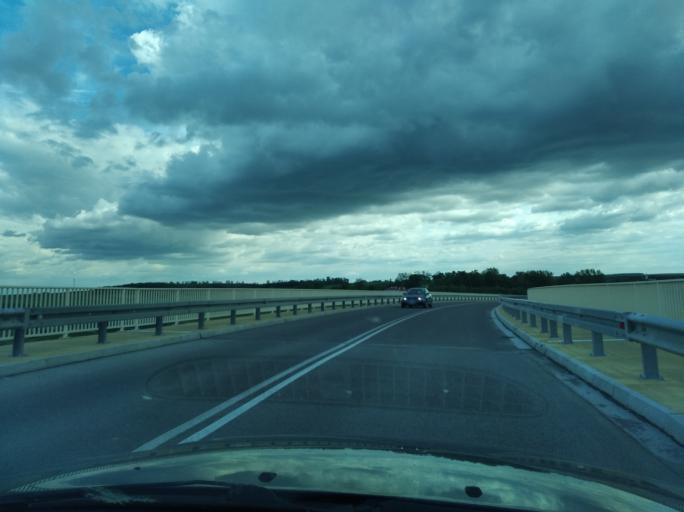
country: PL
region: Subcarpathian Voivodeship
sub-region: Powiat jaroslawski
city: Rokietnica
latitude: 49.9457
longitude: 22.6688
